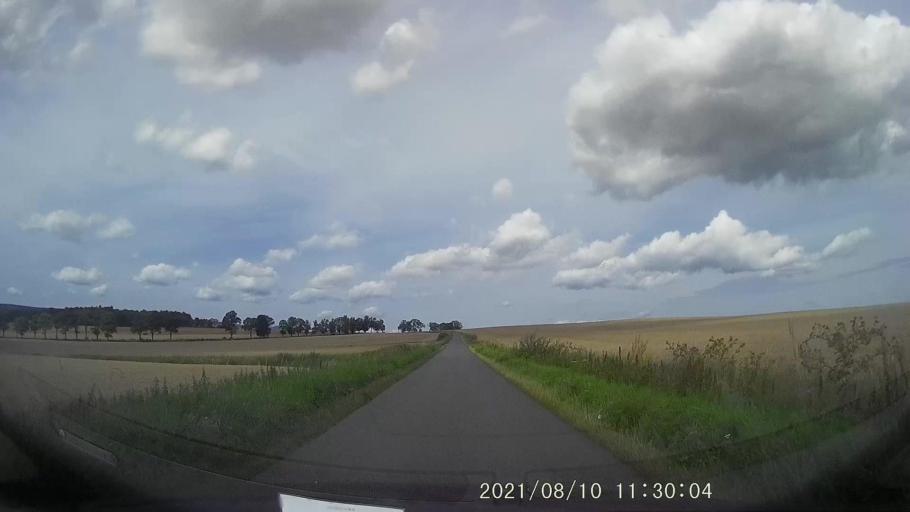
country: PL
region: Lower Silesian Voivodeship
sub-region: Powiat klodzki
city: Polanica-Zdroj
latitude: 50.4484
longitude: 16.5546
